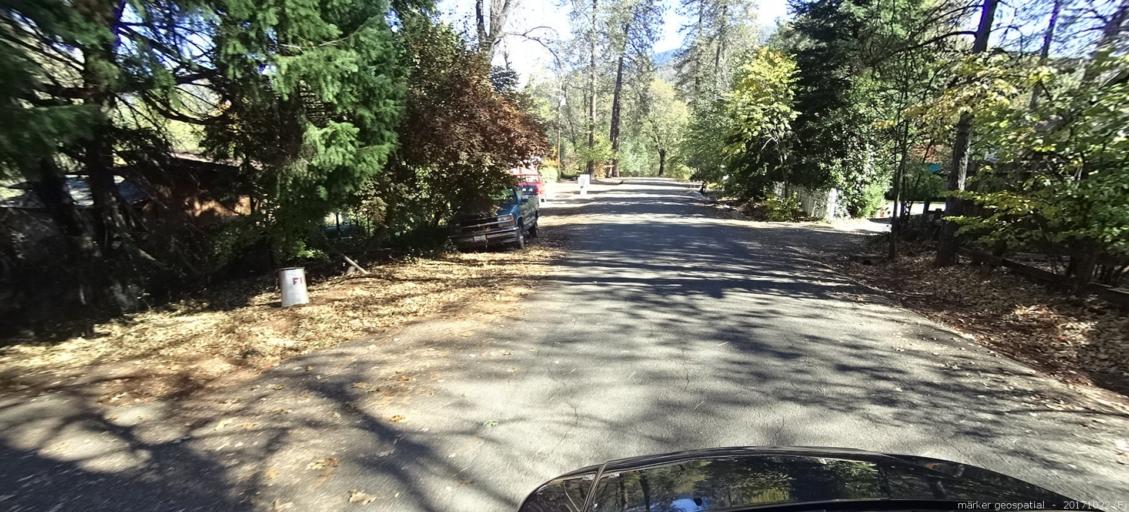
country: US
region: California
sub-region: Shasta County
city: Central Valley (historical)
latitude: 40.9080
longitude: -122.3828
